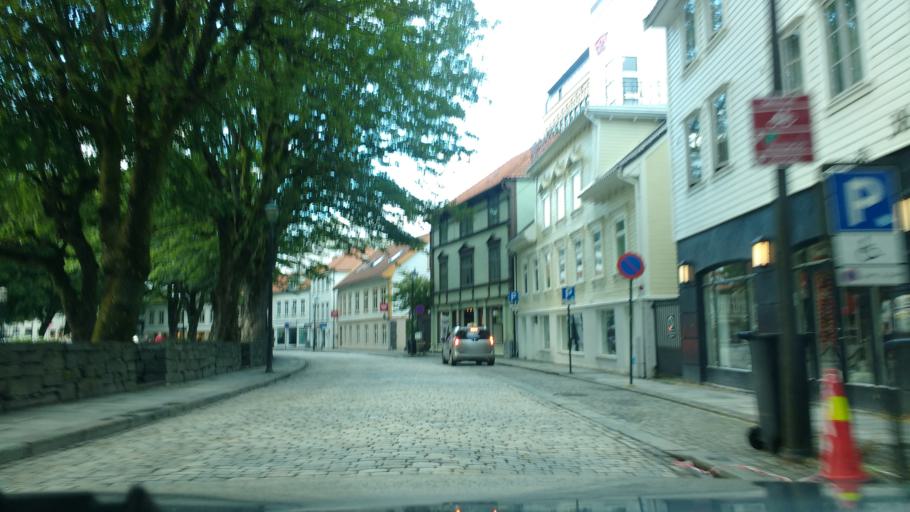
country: NO
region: Rogaland
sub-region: Stavanger
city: Stavanger
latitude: 58.9682
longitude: 5.7351
